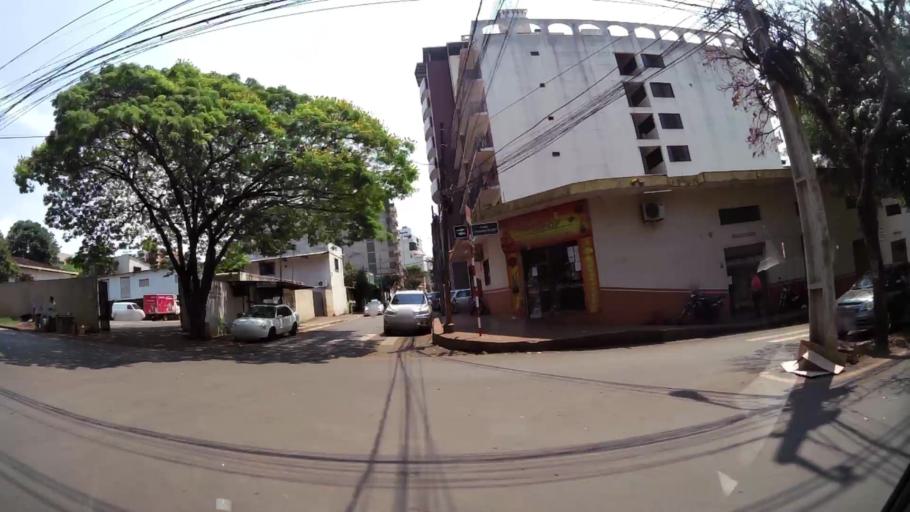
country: PY
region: Alto Parana
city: Ciudad del Este
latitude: -25.5139
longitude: -54.6117
